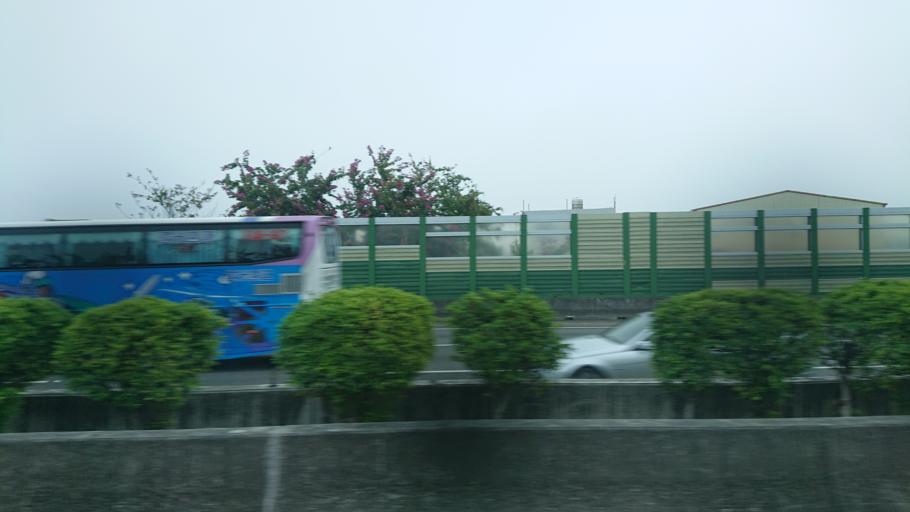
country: TW
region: Taiwan
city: Fengyuan
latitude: 24.3360
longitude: 120.7191
